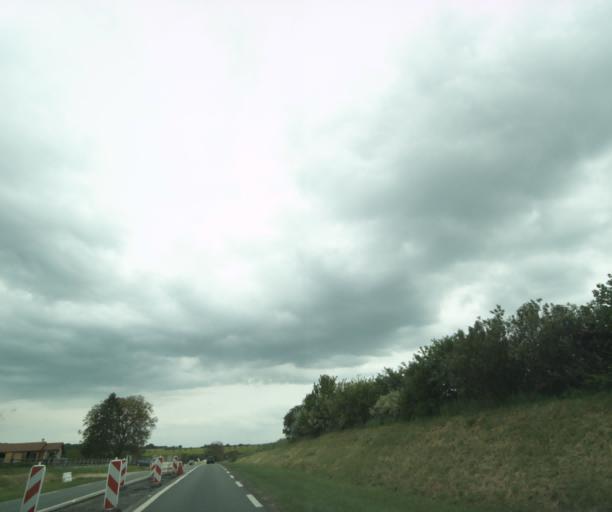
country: FR
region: Ile-de-France
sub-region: Departement des Yvelines
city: Ecquevilly
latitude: 48.9472
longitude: 1.9217
